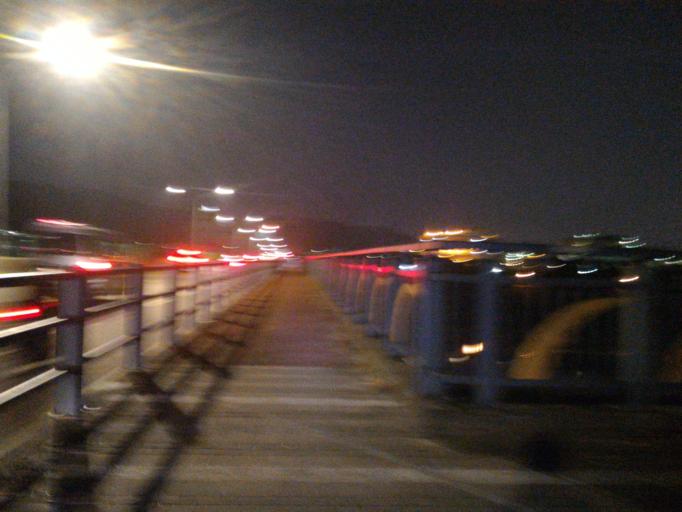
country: TW
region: Taipei
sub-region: Taipei
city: Banqiao
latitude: 24.9669
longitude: 121.4047
